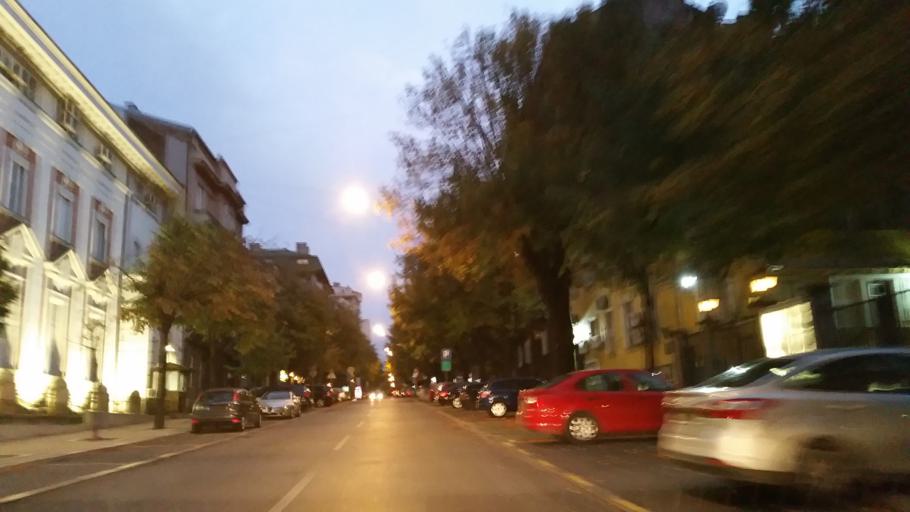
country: RS
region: Central Serbia
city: Belgrade
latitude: 44.8033
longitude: 20.4615
